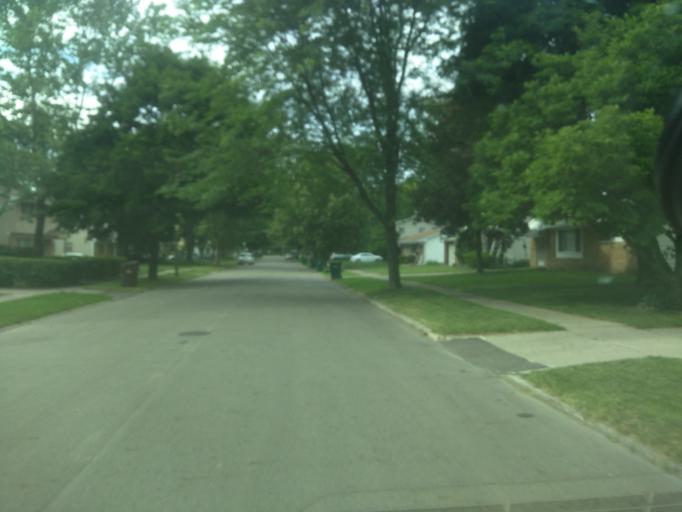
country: US
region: Michigan
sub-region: Eaton County
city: Waverly
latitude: 42.6930
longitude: -84.5940
